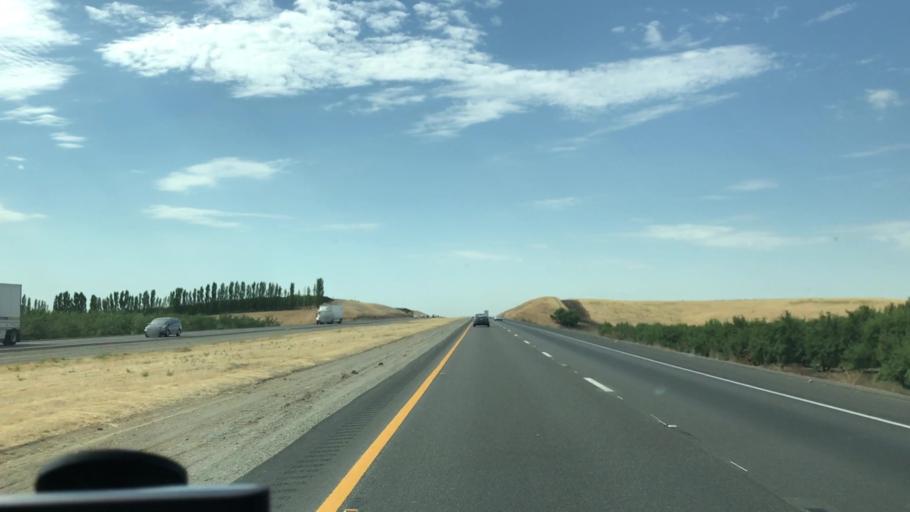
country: US
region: California
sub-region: Stanislaus County
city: Patterson
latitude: 37.3725
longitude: -121.1255
